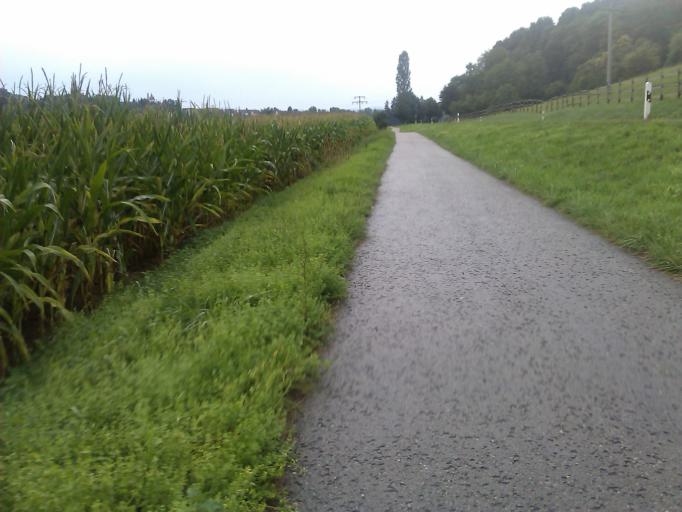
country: DE
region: Baden-Wuerttemberg
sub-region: Regierungsbezirk Stuttgart
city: Neckartenzlingen
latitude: 48.5720
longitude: 9.2266
